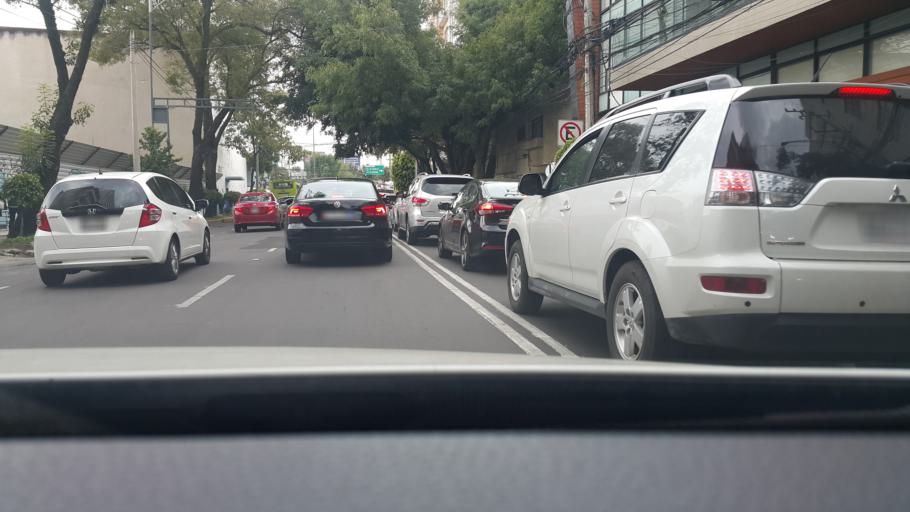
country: MX
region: Mexico City
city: Coyoacan
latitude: 19.3615
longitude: -99.1720
